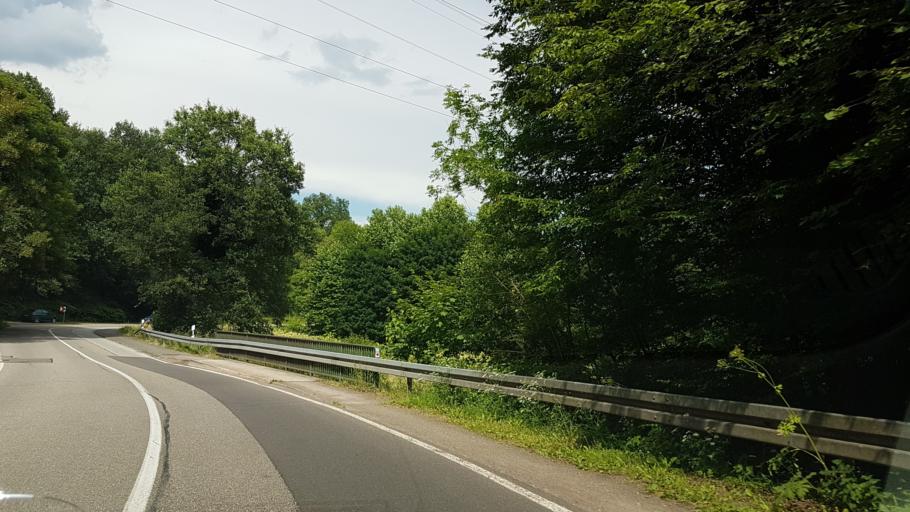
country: DE
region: Saarland
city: Saarbrucken
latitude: 49.2646
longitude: 6.9823
